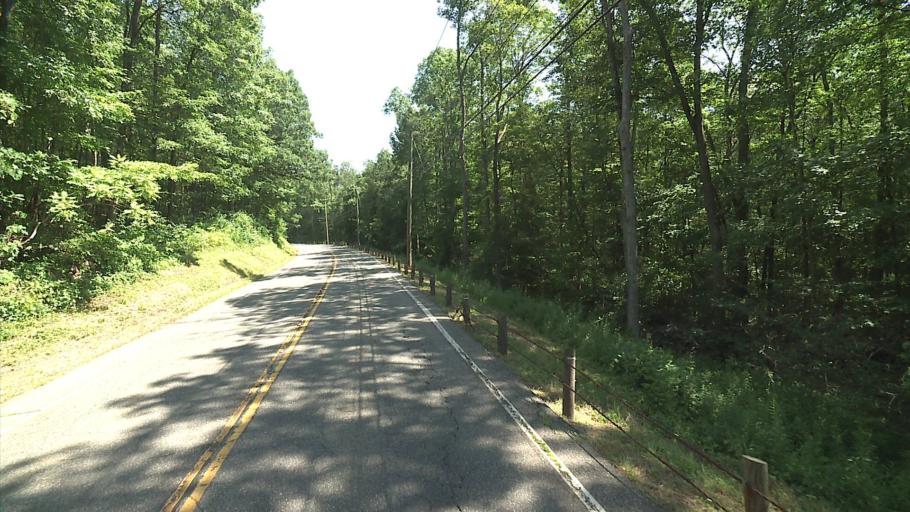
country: US
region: Connecticut
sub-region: Litchfield County
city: New Preston
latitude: 41.7321
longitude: -73.3398
